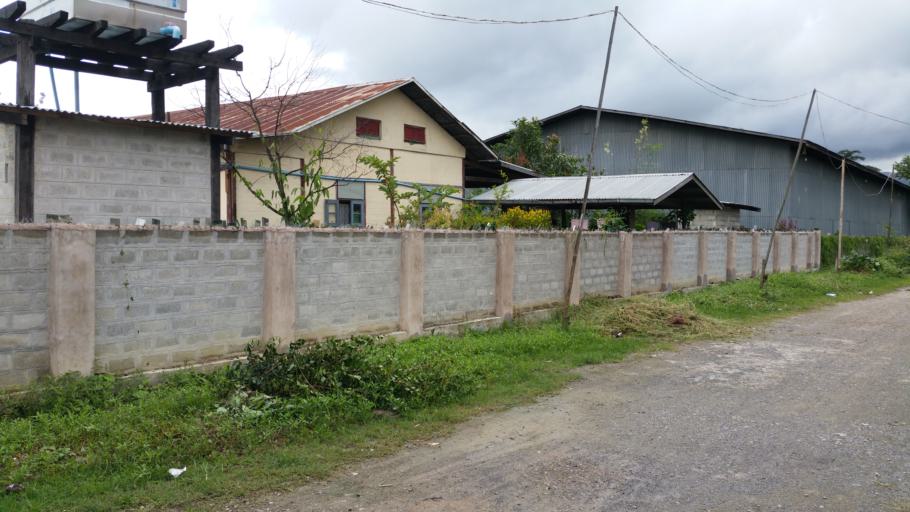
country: MM
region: Shan
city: Taunggyi
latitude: 20.6618
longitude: 96.9369
